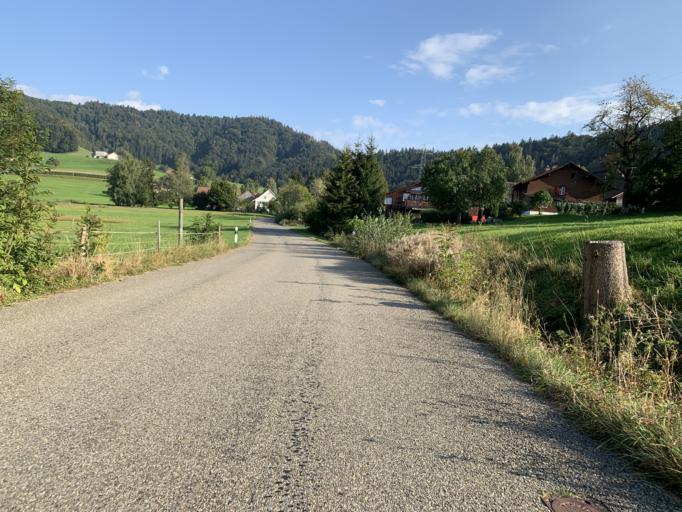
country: CH
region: Zurich
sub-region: Bezirk Hinwil
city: Baretswil
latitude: 47.3225
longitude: 8.8704
